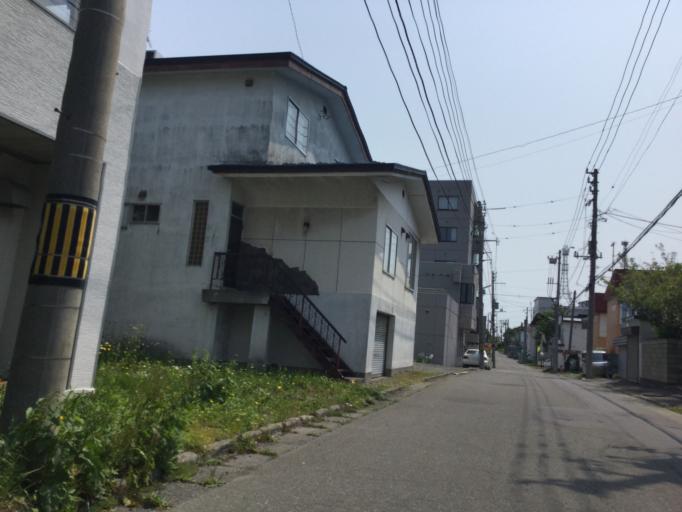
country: JP
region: Hokkaido
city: Wakkanai
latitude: 45.3996
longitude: 141.6787
